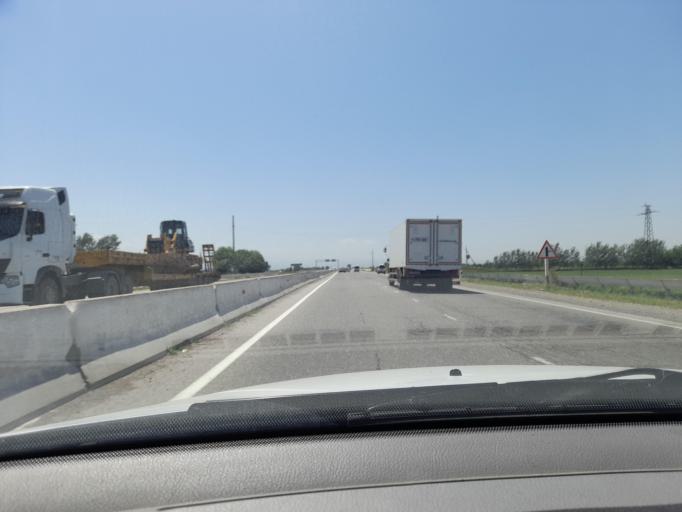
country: UZ
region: Jizzax
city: Paxtakor
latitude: 40.2424
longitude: 68.0076
